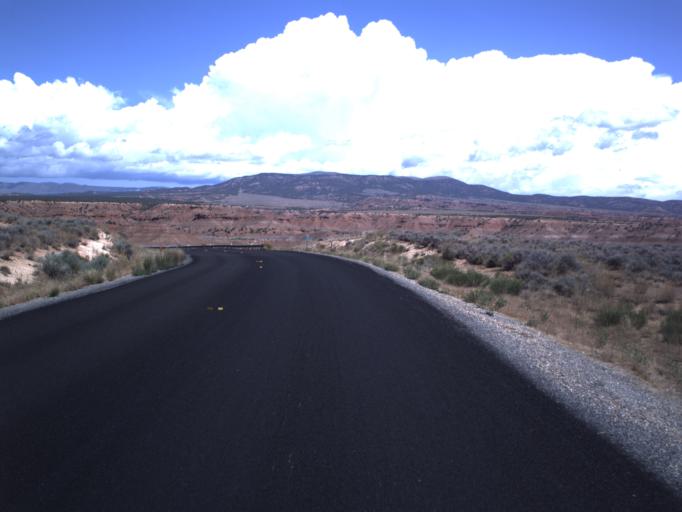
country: US
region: Utah
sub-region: Uintah County
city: Maeser
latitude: 40.4099
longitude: -109.7640
